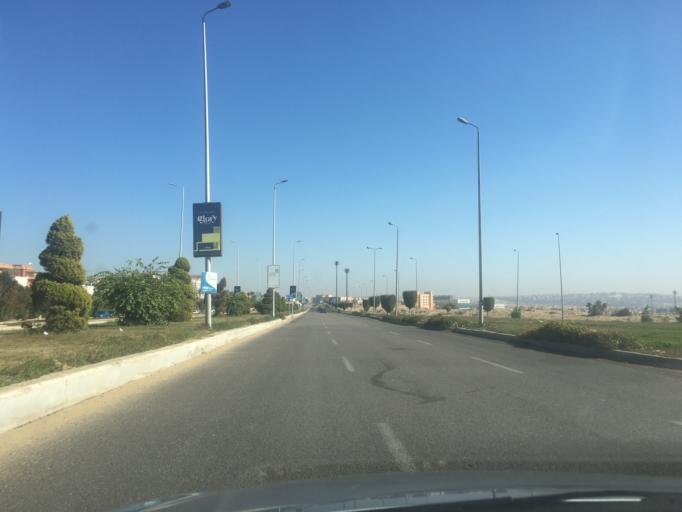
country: EG
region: Al Jizah
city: Awsim
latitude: 30.0193
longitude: 30.9910
